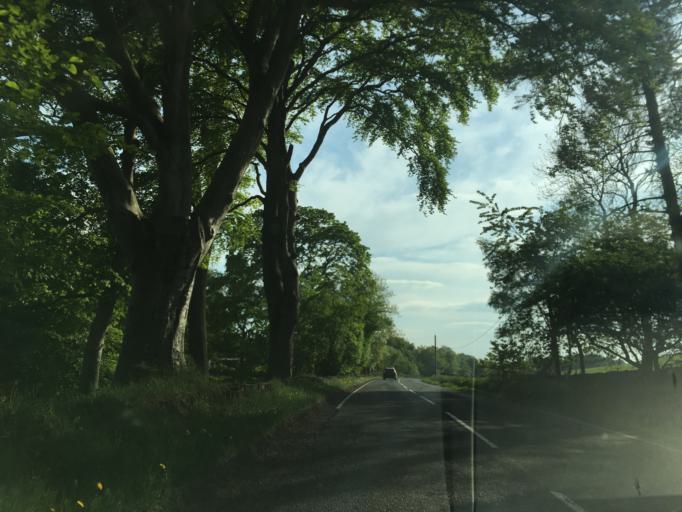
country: GB
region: Scotland
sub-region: The Scottish Borders
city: West Linton
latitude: 55.7001
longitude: -3.3663
